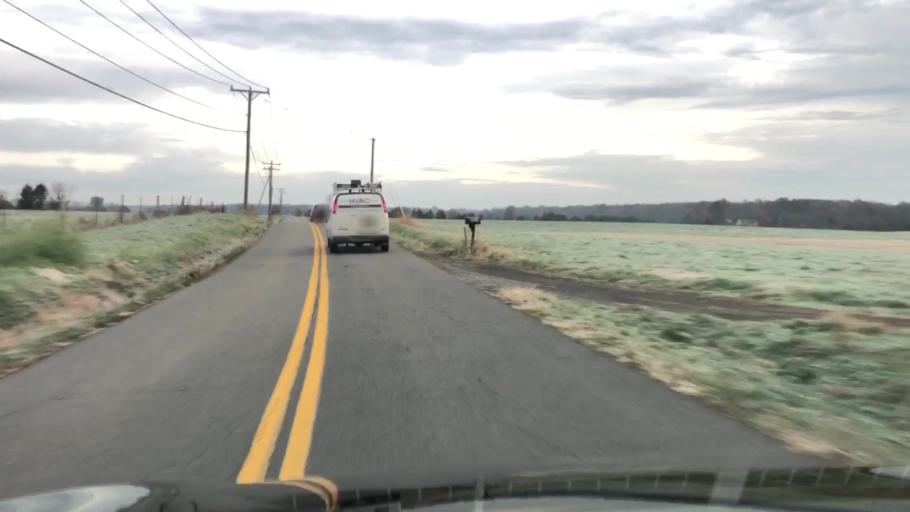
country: US
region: Virginia
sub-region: Prince William County
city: Nokesville
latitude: 38.6620
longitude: -77.6738
